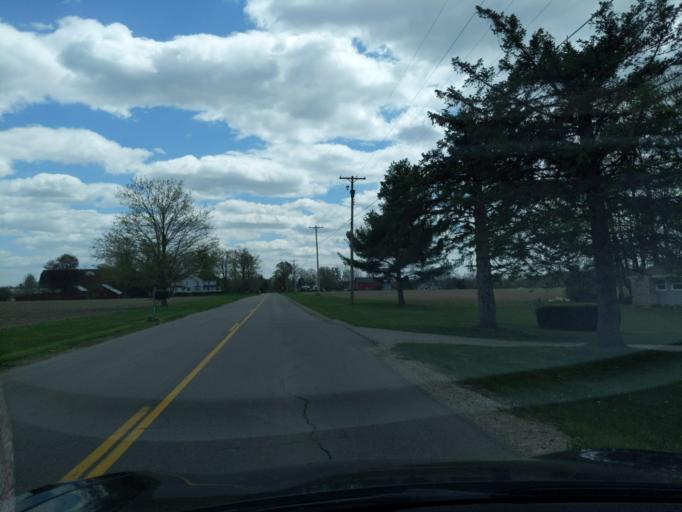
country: US
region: Michigan
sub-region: Eaton County
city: Dimondale
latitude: 42.6443
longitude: -84.6128
